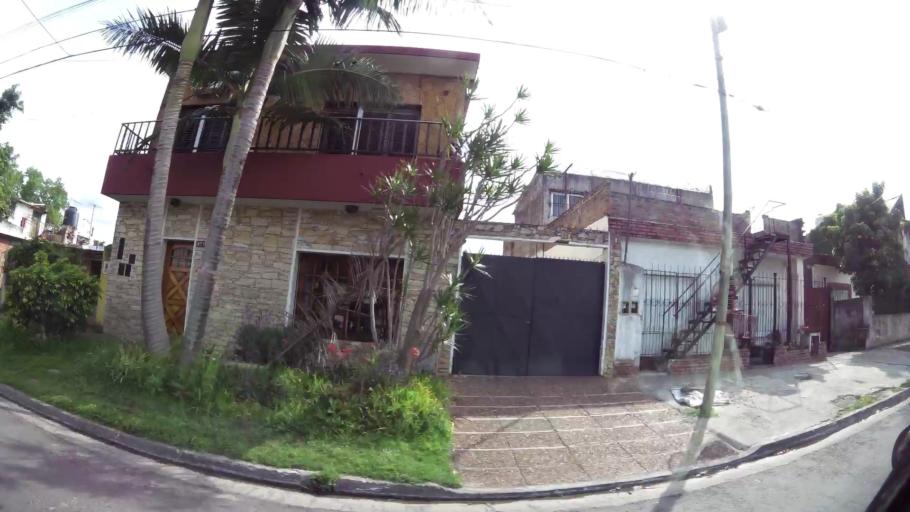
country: AR
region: Buenos Aires
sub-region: Partido de Quilmes
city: Quilmes
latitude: -34.7751
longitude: -58.2581
